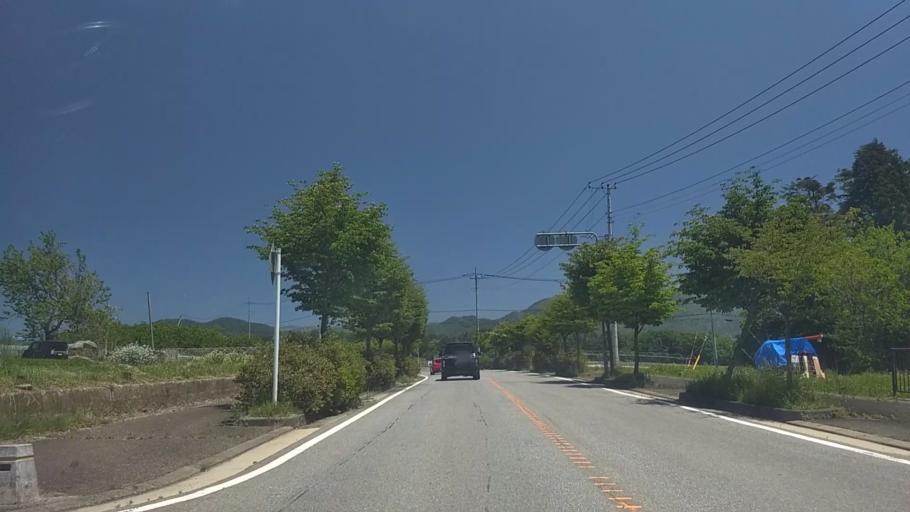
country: JP
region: Yamanashi
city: Nirasaki
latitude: 35.8400
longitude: 138.4324
